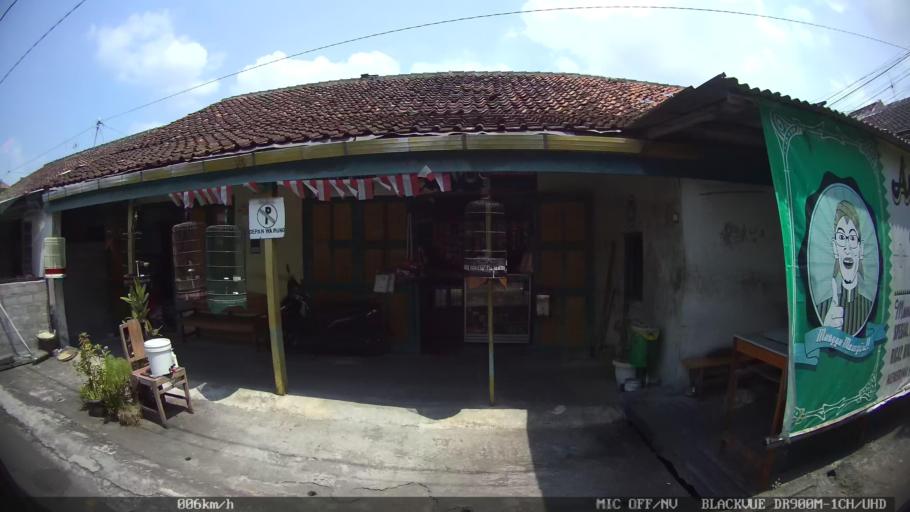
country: ID
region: Daerah Istimewa Yogyakarta
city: Yogyakarta
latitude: -7.8048
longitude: 110.4002
